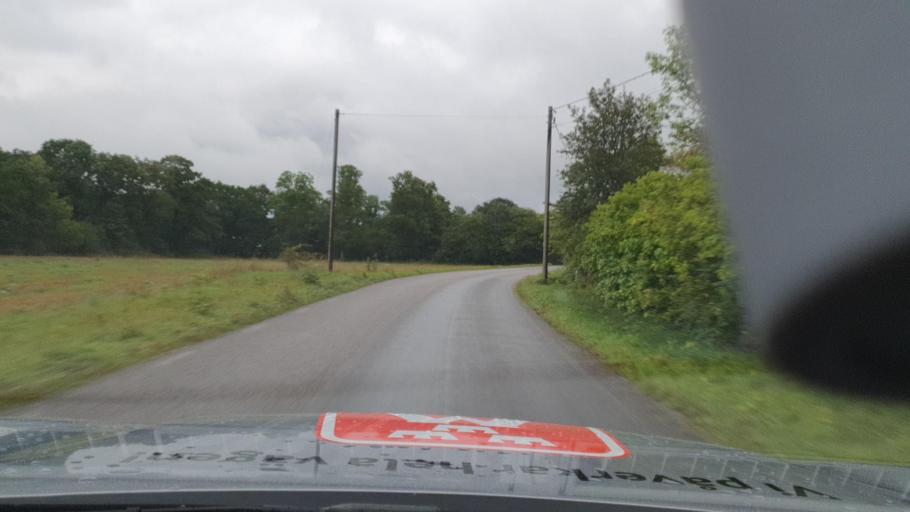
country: SE
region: Gotland
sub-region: Gotland
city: Visby
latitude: 57.7799
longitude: 18.5033
